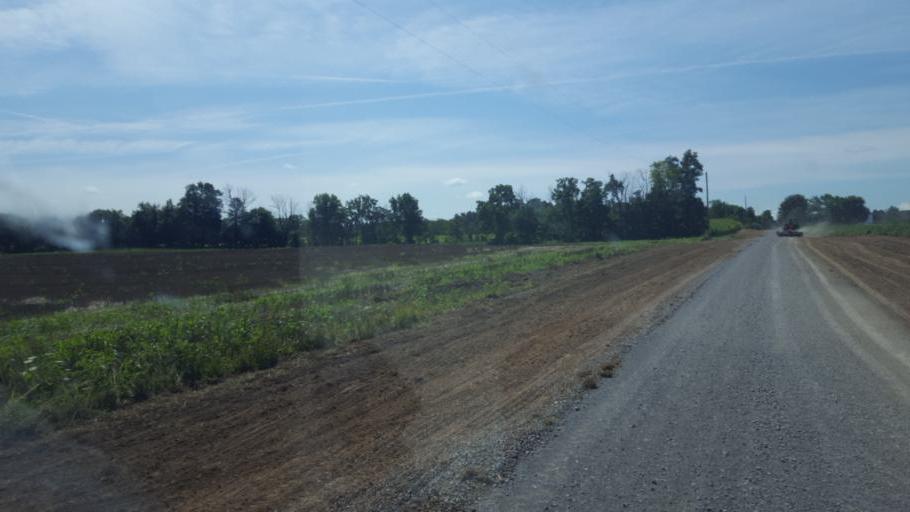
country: US
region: Ohio
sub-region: Knox County
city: Centerburg
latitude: 40.4457
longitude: -82.7171
